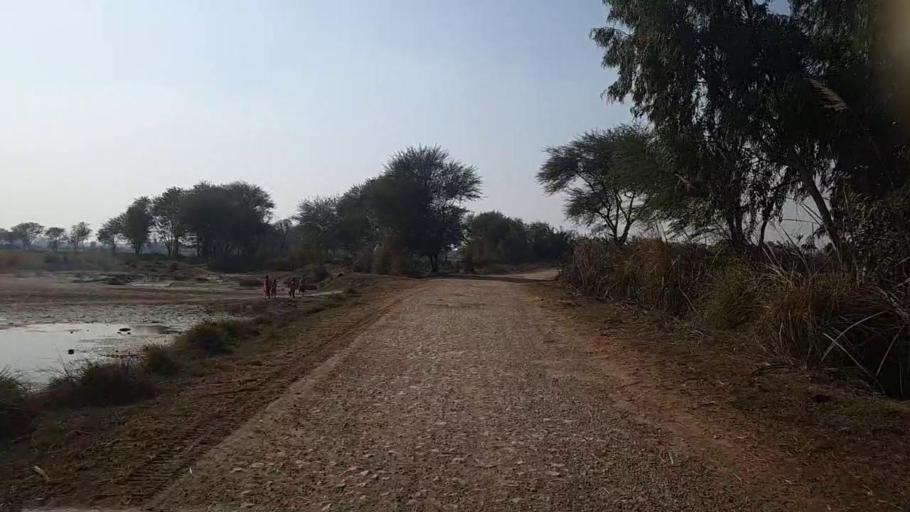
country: PK
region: Sindh
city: Mirpur Mathelo
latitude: 27.9022
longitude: 69.6236
